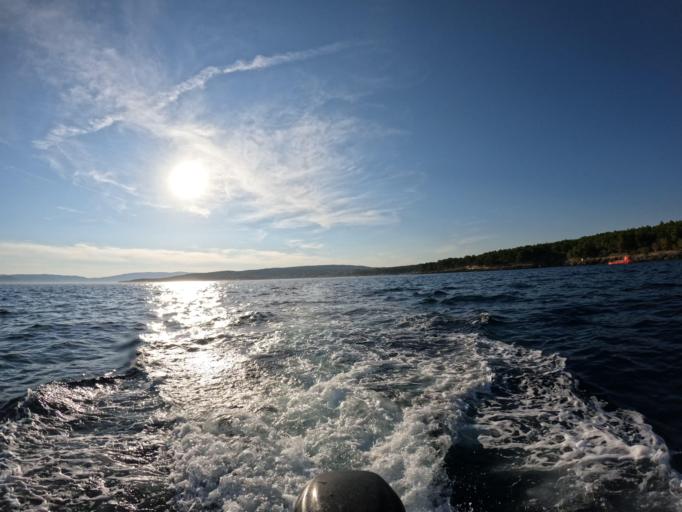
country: HR
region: Primorsko-Goranska
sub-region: Grad Krk
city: Krk
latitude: 45.0173
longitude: 14.5971
